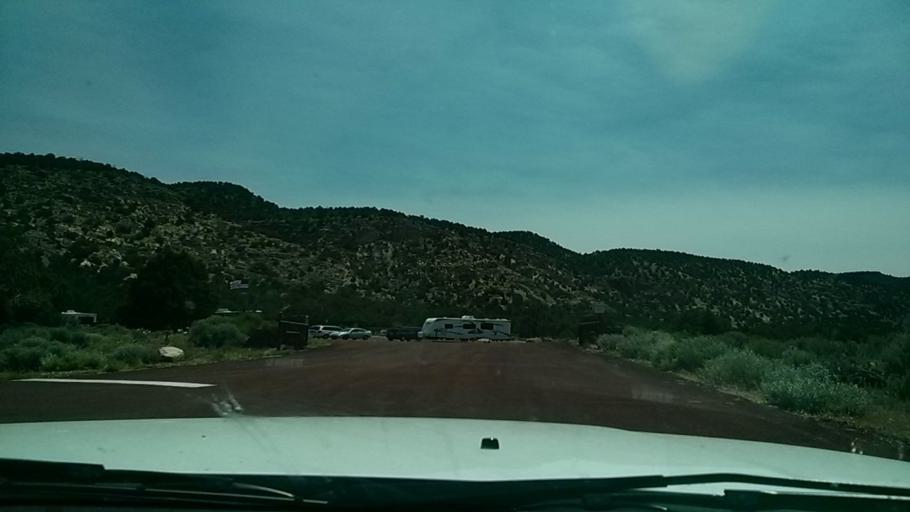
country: US
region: Utah
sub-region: Washington County
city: Toquerville
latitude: 37.4543
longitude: -113.2269
